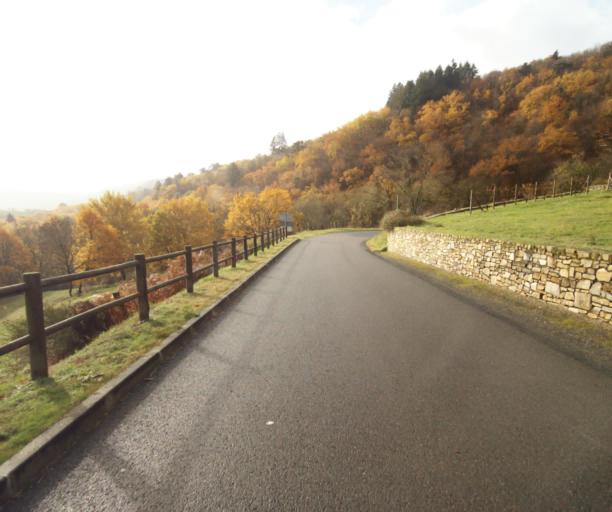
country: FR
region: Limousin
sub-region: Departement de la Correze
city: Cornil
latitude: 45.2125
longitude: 1.6497
